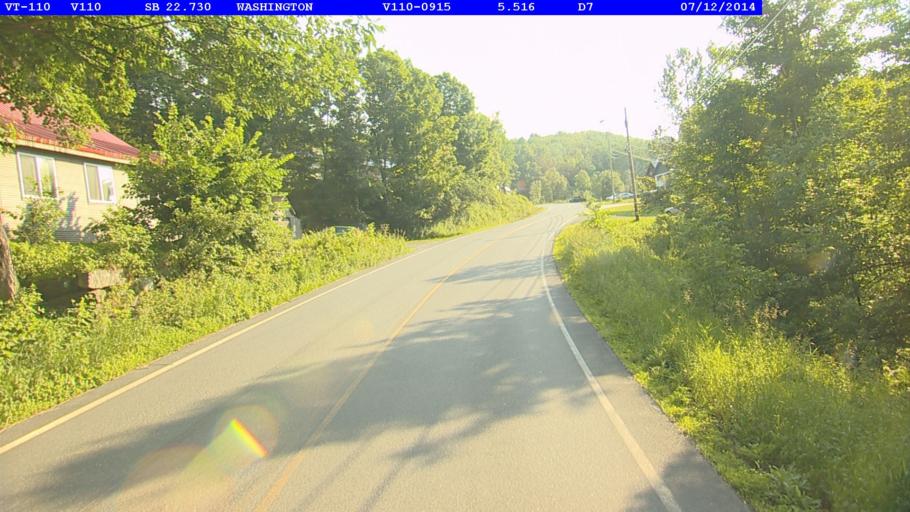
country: US
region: Vermont
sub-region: Washington County
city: South Barre
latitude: 44.1034
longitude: -72.4345
